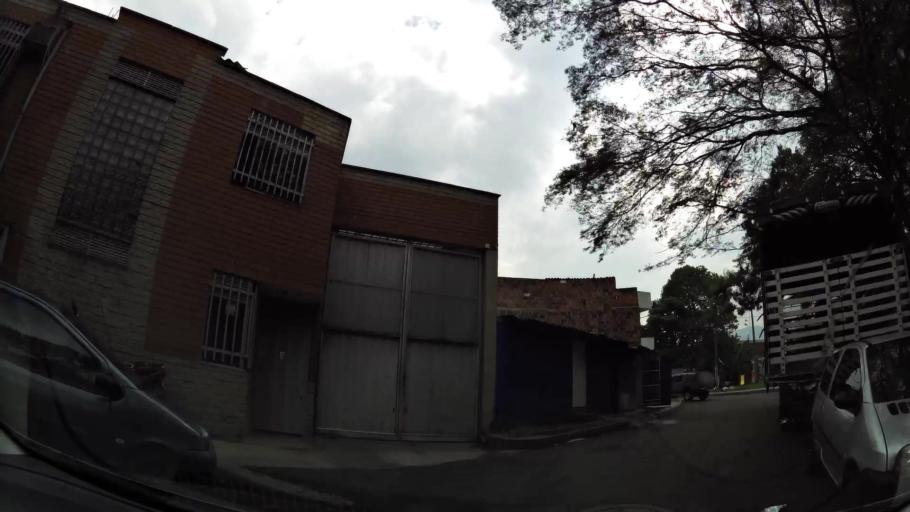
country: CO
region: Antioquia
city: Itagui
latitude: 6.1943
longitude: -75.5896
